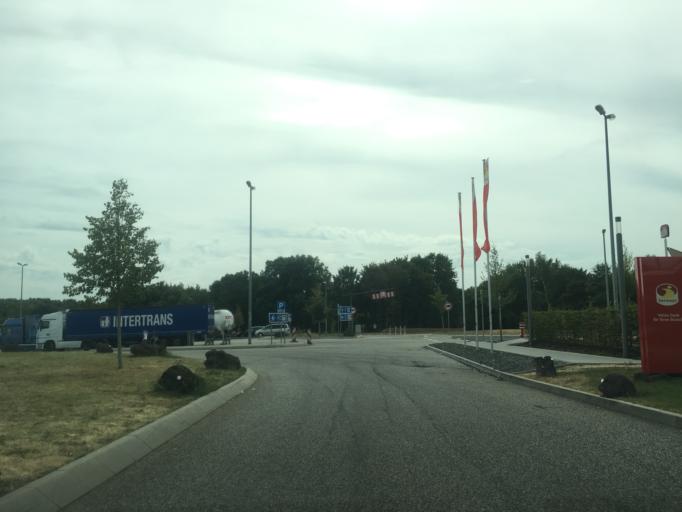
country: DE
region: Rheinland-Pfalz
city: Daxweiler
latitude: 49.9644
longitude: 7.7656
